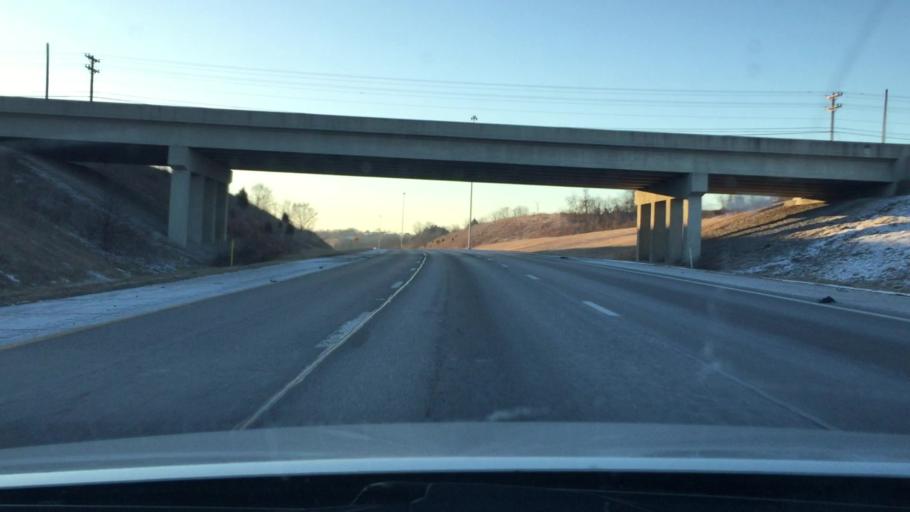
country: US
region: Kentucky
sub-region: Grant County
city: Williamstown
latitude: 38.6468
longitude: -84.5877
